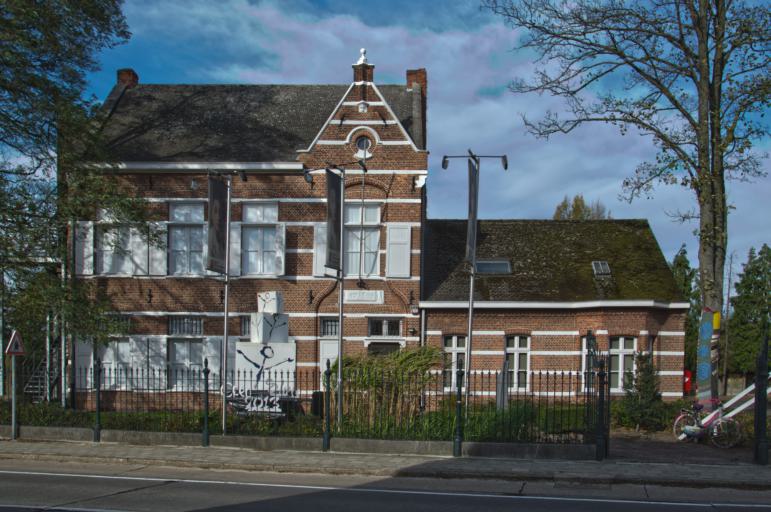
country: BE
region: Flanders
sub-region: Provincie Antwerpen
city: Mol
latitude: 51.2111
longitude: 5.1338
